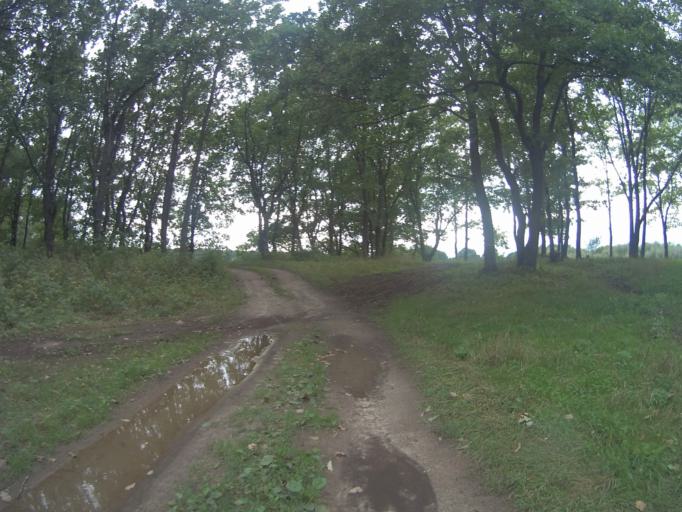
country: RU
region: Vladimir
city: Raduzhnyy
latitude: 56.0337
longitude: 40.2800
